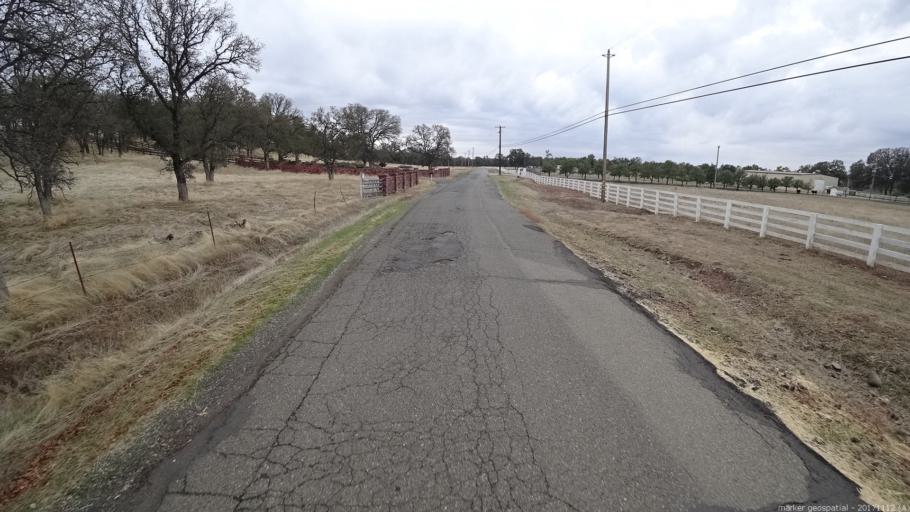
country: US
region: California
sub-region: Shasta County
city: Palo Cedro
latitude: 40.5328
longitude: -122.2265
